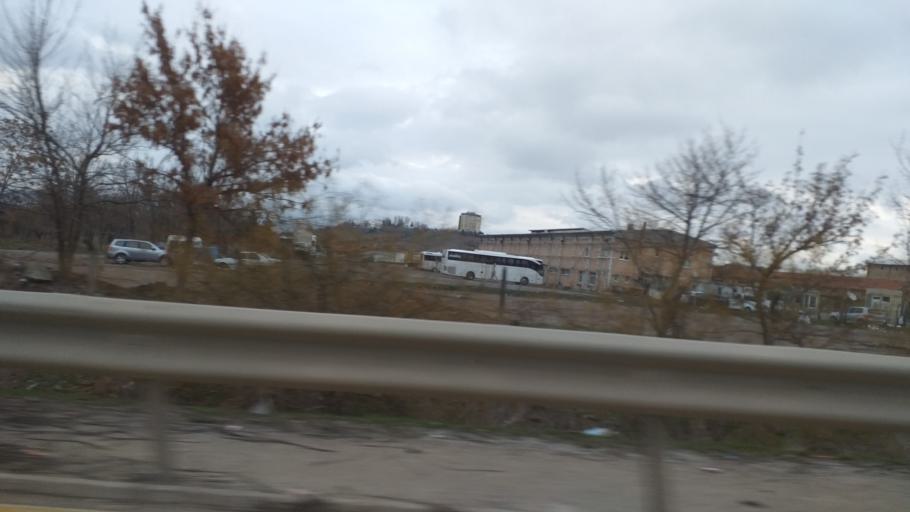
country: TR
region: Ankara
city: Ankara
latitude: 39.9182
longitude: 32.7875
